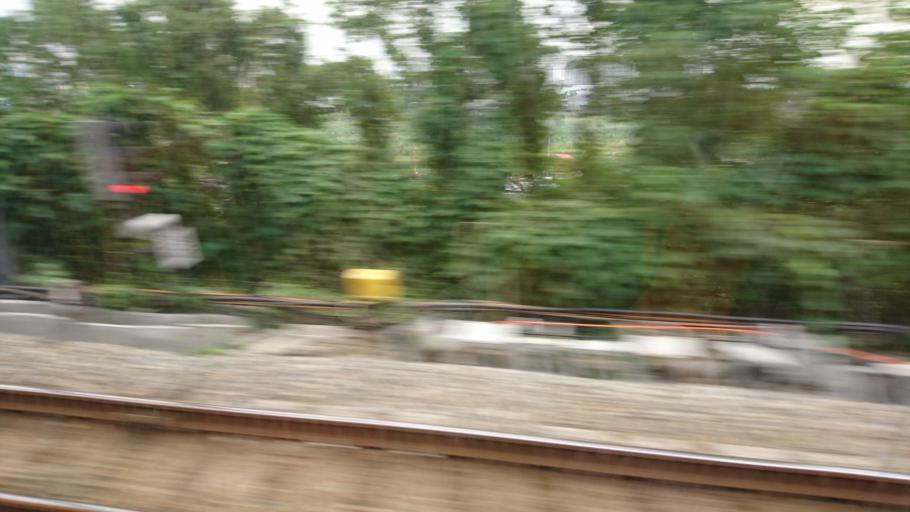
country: TW
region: Taiwan
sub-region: Hsinchu
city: Zhubei
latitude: 24.8549
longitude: 121.0081
